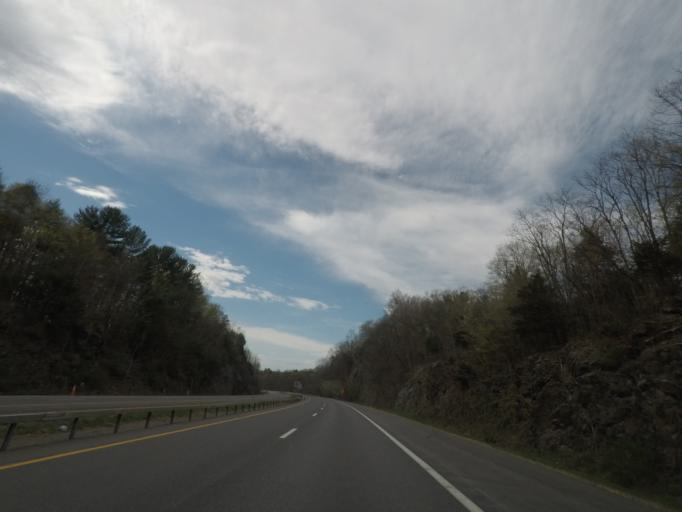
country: US
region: New York
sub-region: Greene County
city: Jefferson Heights
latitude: 42.2467
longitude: -73.8933
